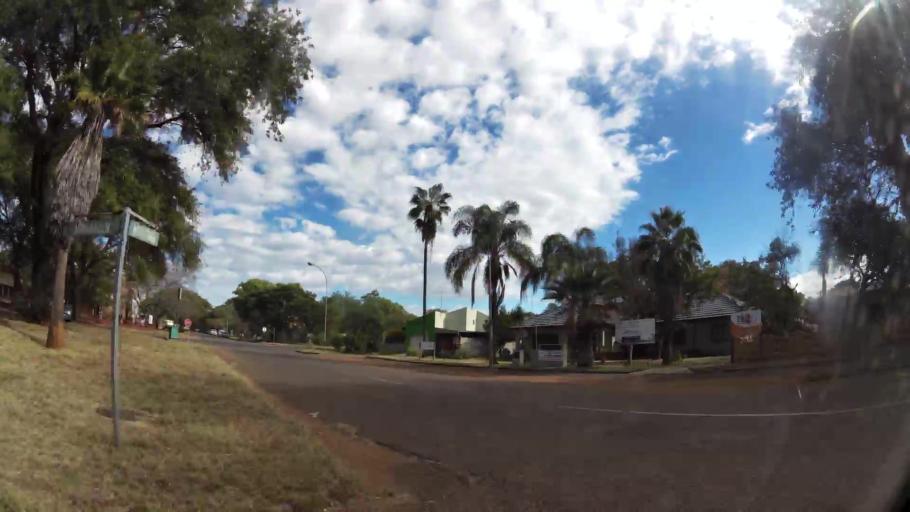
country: ZA
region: Limpopo
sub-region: Waterberg District Municipality
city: Bela-Bela
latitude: -24.8830
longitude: 28.2928
